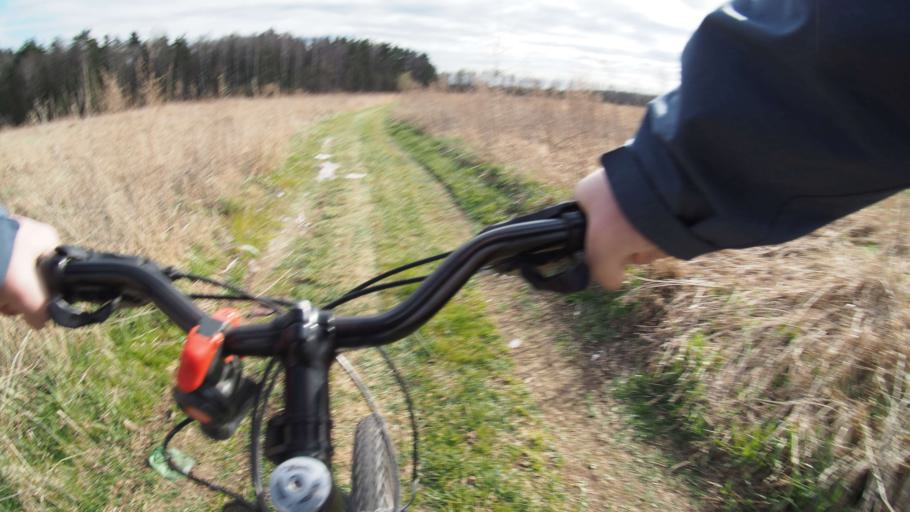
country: RU
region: Moskovskaya
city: Ramenskoye
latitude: 55.6001
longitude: 38.2891
